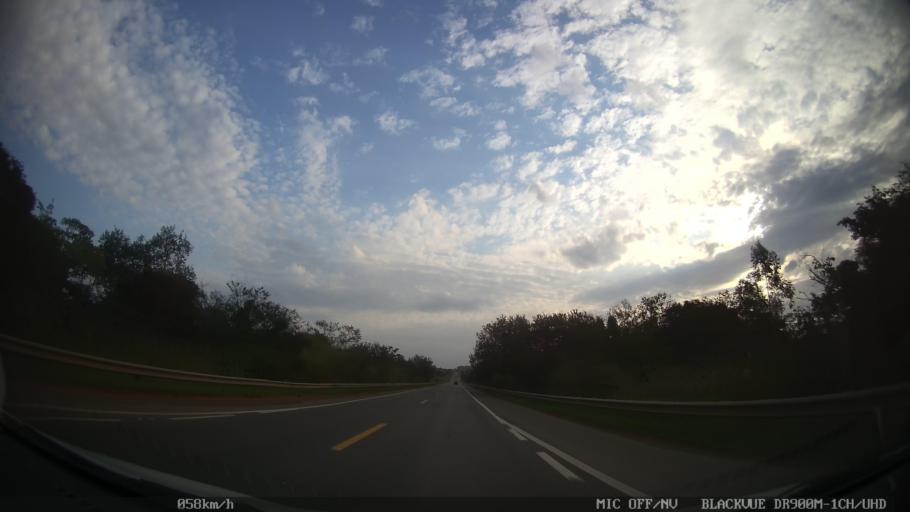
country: BR
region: Sao Paulo
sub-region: Cosmopolis
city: Cosmopolis
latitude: -22.6291
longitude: -47.2800
